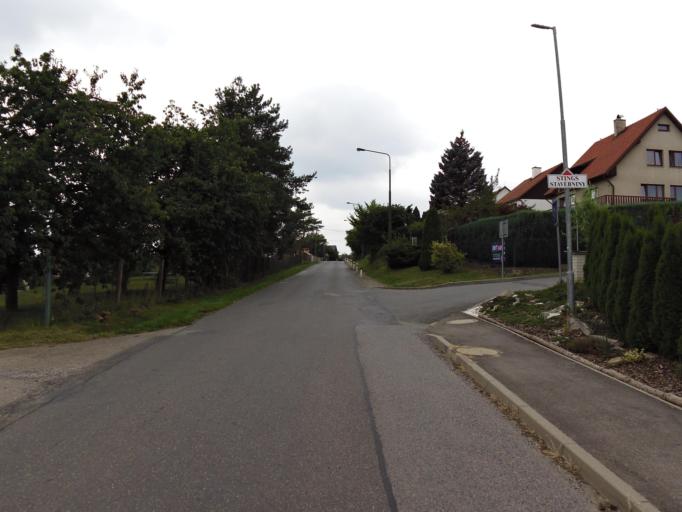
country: CZ
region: Central Bohemia
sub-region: Okres Benesov
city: Pysely
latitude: 49.8743
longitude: 14.6828
